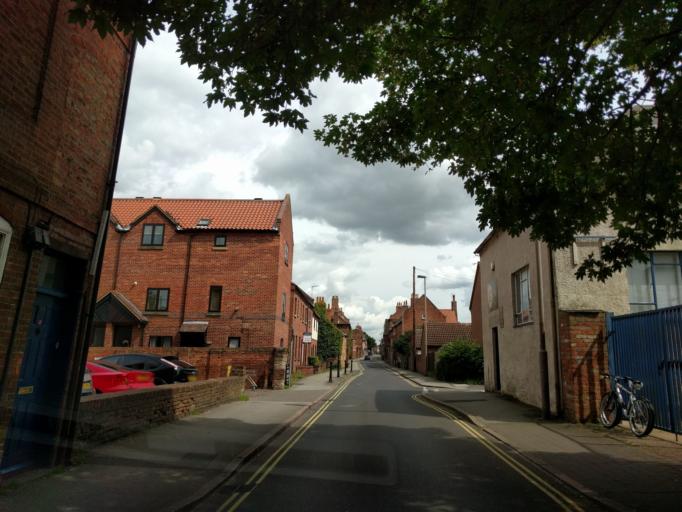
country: GB
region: England
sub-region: Nottinghamshire
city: Newark on Trent
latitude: 53.0745
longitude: -0.8163
